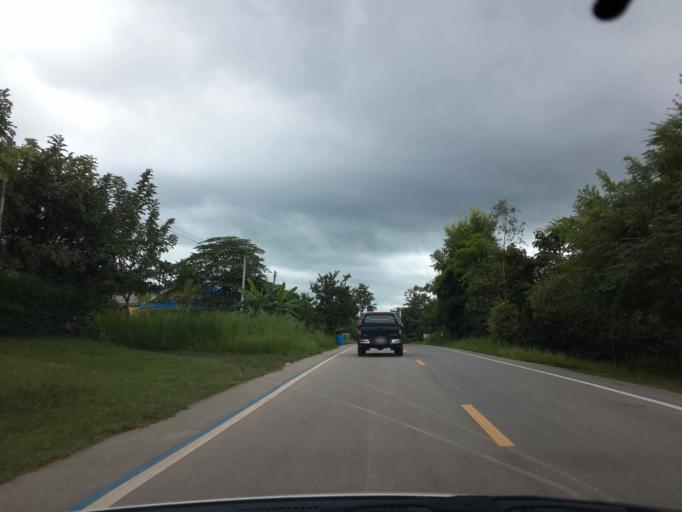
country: TH
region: Ratchaburi
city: Suan Phueng
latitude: 13.6474
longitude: 99.2119
